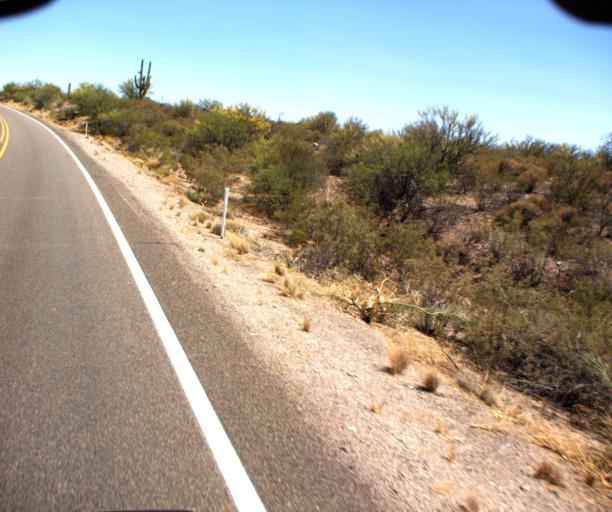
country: US
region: Arizona
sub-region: Pima County
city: Catalina
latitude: 32.6756
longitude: -111.0684
